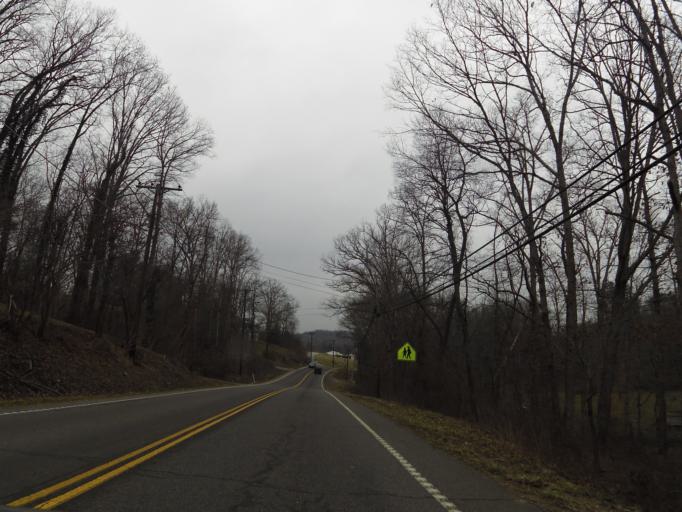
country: US
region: Tennessee
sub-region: Morgan County
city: Wartburg
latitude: 36.2390
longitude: -84.6711
